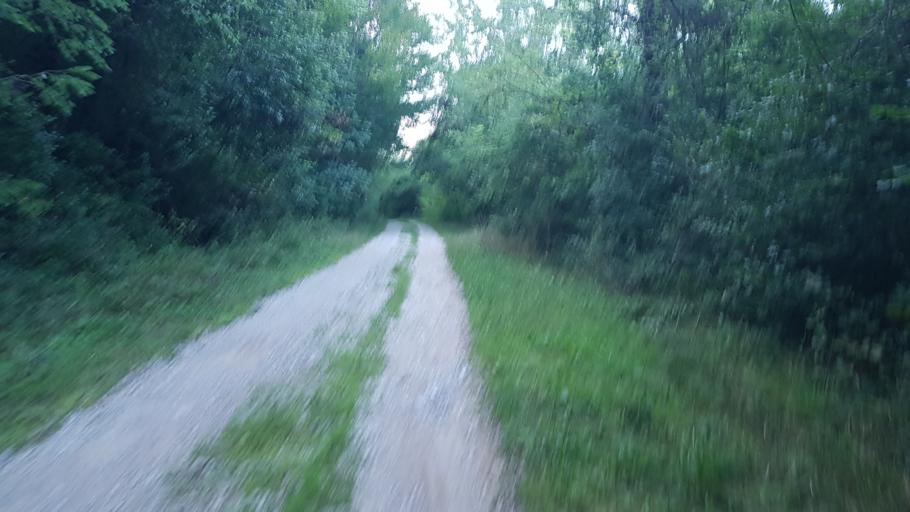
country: IT
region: Friuli Venezia Giulia
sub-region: Provincia di Gorizia
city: Mossa
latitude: 45.9430
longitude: 13.5360
